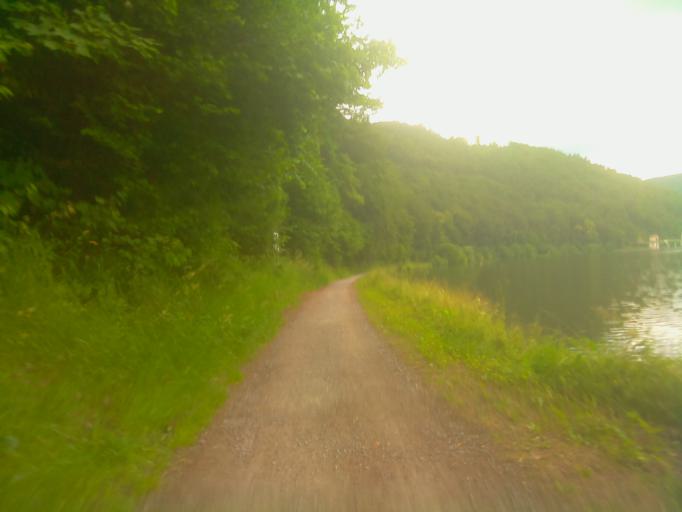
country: DE
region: Hesse
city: Neckarsteinach
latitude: 49.3951
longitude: 8.8488
